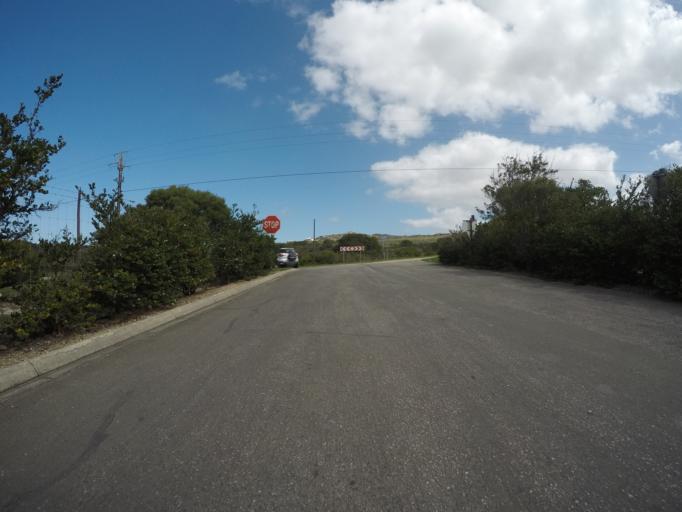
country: ZA
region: Western Cape
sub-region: Eden District Municipality
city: Mossel Bay
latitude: -34.1441
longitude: 22.0883
